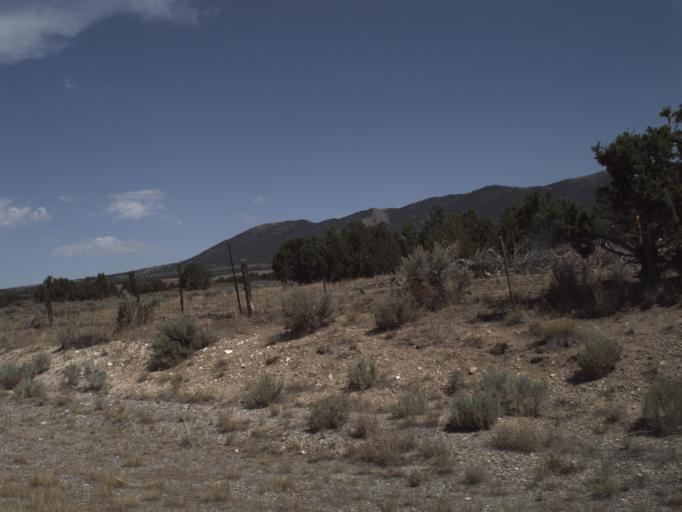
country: US
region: Utah
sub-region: Utah County
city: Genola
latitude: 39.9401
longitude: -112.1864
